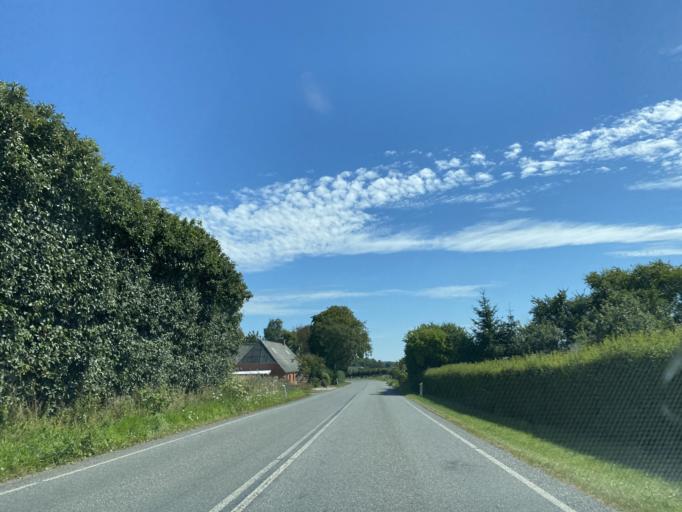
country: DK
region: South Denmark
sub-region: Faaborg-Midtfyn Kommune
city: Ringe
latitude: 55.2088
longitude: 10.3979
